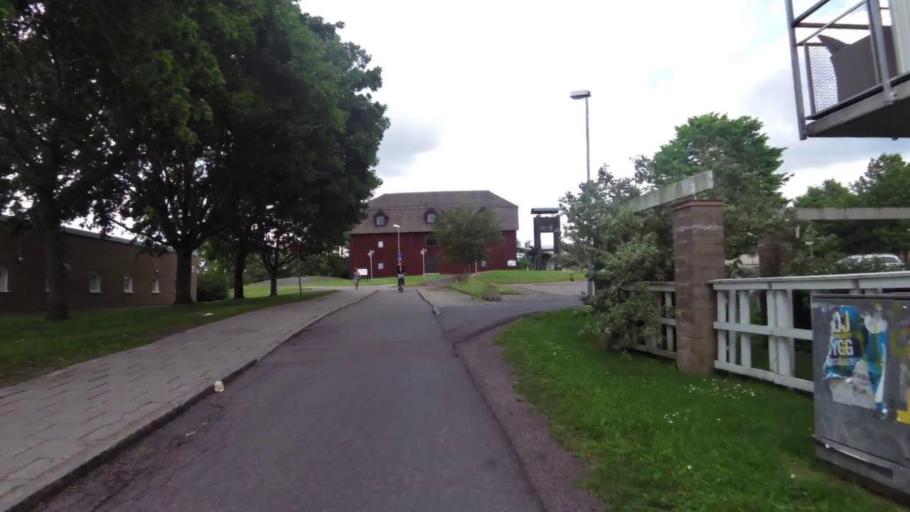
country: SE
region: OEstergoetland
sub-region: Linkopings Kommun
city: Malmslatt
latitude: 58.4097
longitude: 15.5658
